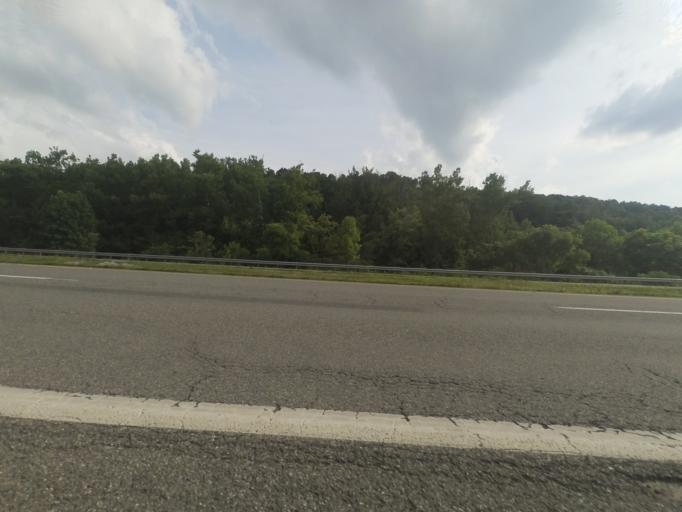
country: US
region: West Virginia
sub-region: Cabell County
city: Huntington
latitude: 38.3948
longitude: -82.4105
